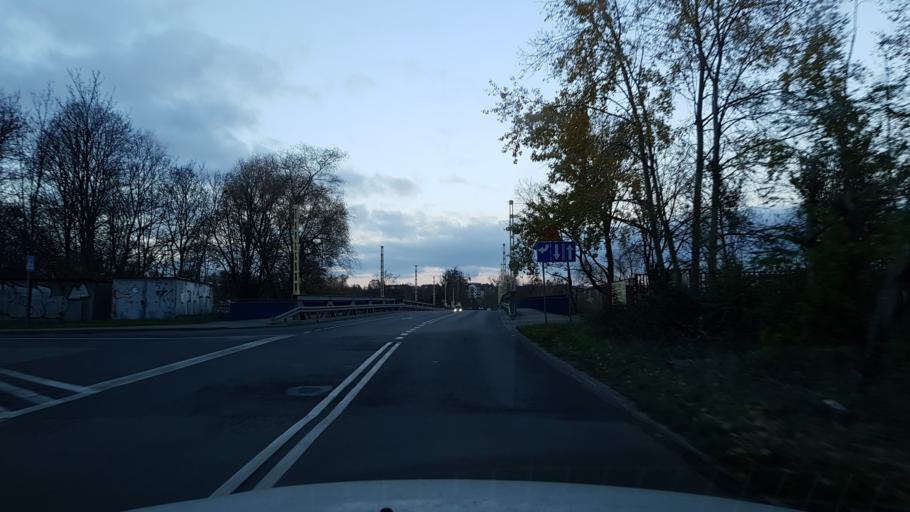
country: PL
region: West Pomeranian Voivodeship
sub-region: Szczecin
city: Szczecin
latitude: 53.4495
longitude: 14.5778
